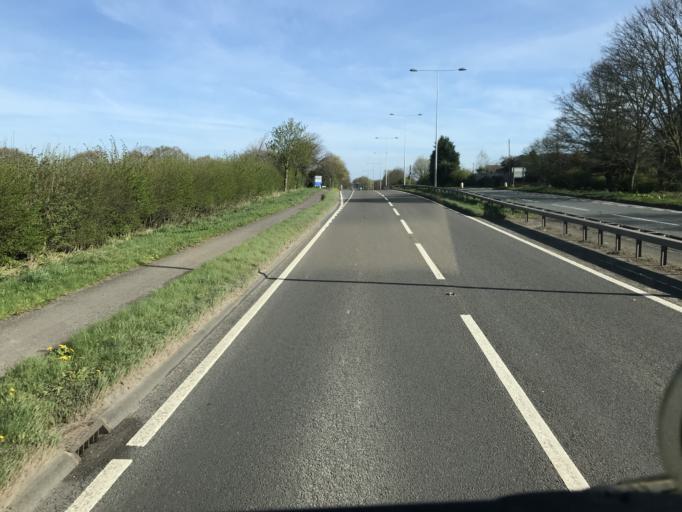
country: GB
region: England
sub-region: Cheshire West and Chester
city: Marston
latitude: 53.2595
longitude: -2.4611
